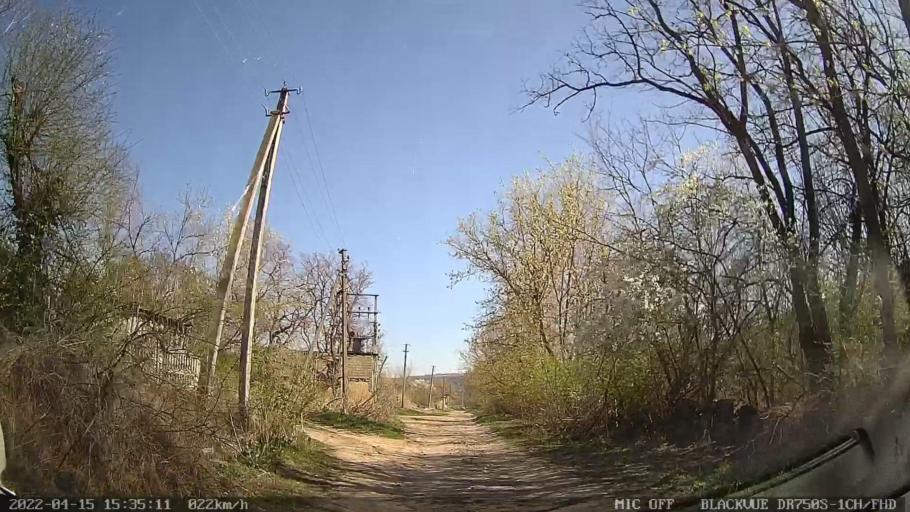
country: MD
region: Raionul Ocnita
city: Otaci
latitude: 48.3455
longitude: 27.9303
